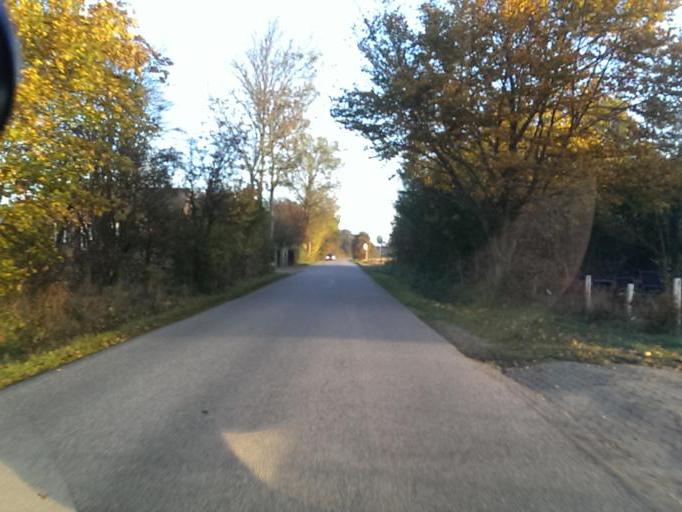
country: DK
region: South Denmark
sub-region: Esbjerg Kommune
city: Tjaereborg
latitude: 55.4769
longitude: 8.6312
